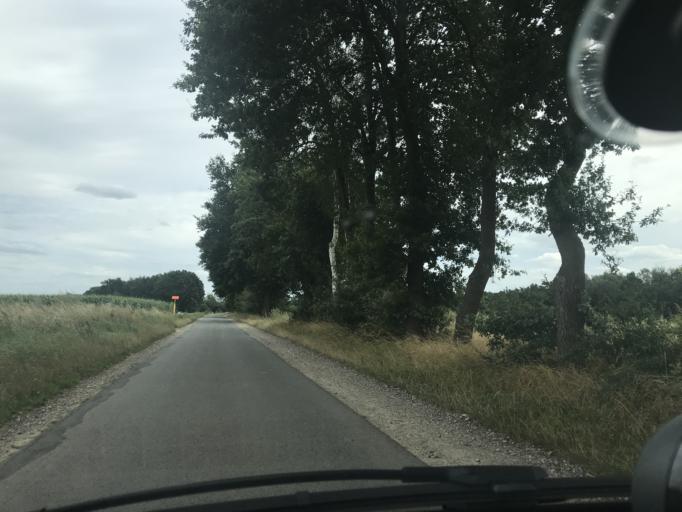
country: DE
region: Lower Saxony
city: Moisburg
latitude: 53.4027
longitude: 9.7104
